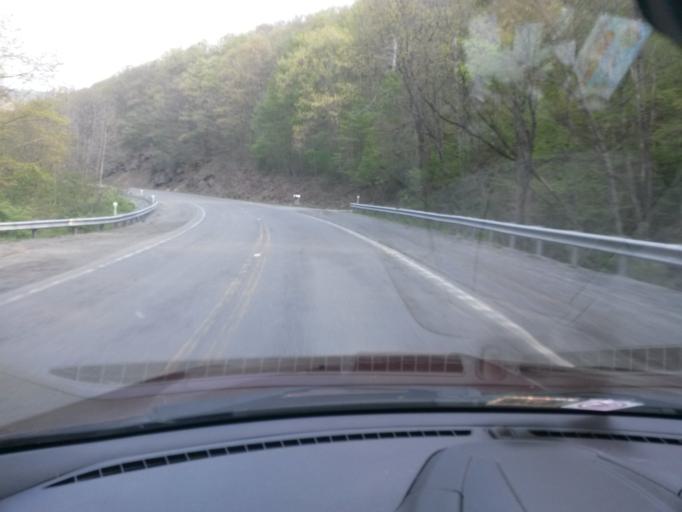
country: US
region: Virginia
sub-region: Highland County
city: Monterey
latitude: 38.5587
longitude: -79.8303
